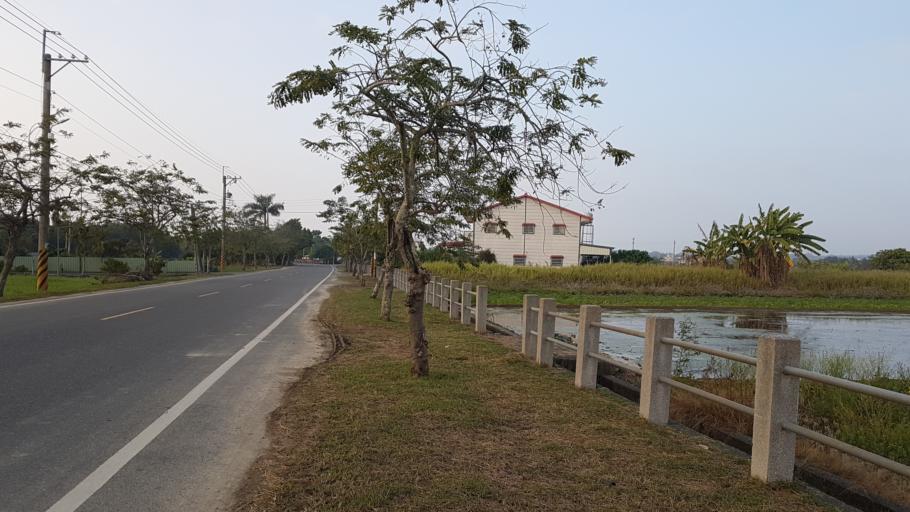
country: TW
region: Taiwan
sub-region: Chiayi
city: Jiayi Shi
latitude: 23.3715
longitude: 120.4499
